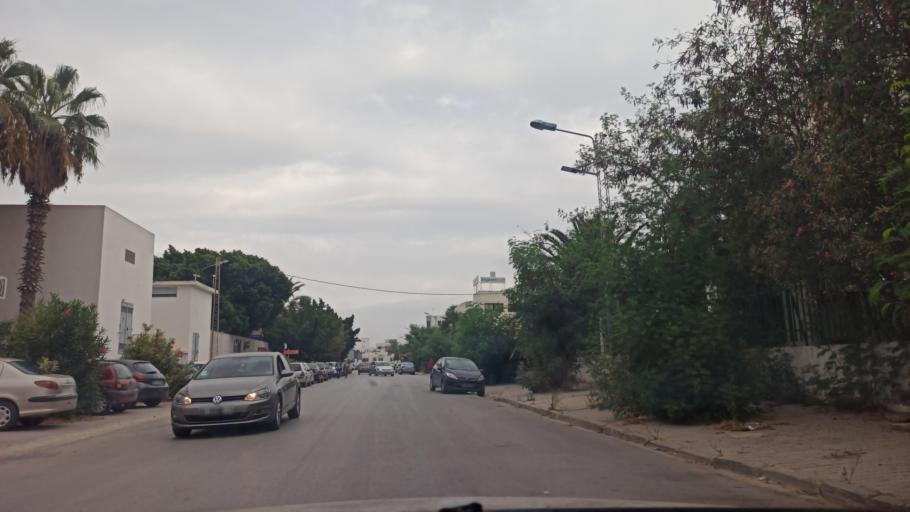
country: TN
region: Ariana
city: Ariana
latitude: 36.8511
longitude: 10.2085
